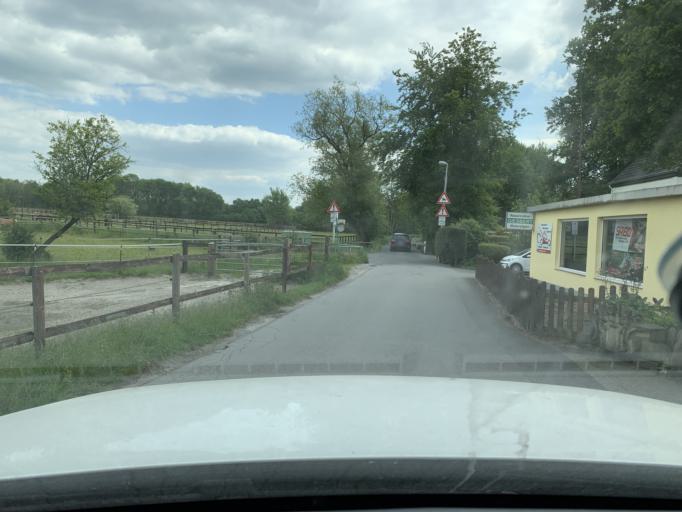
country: DE
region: North Rhine-Westphalia
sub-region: Regierungsbezirk Dusseldorf
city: Muelheim (Ruhr)
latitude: 51.3843
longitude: 6.8676
